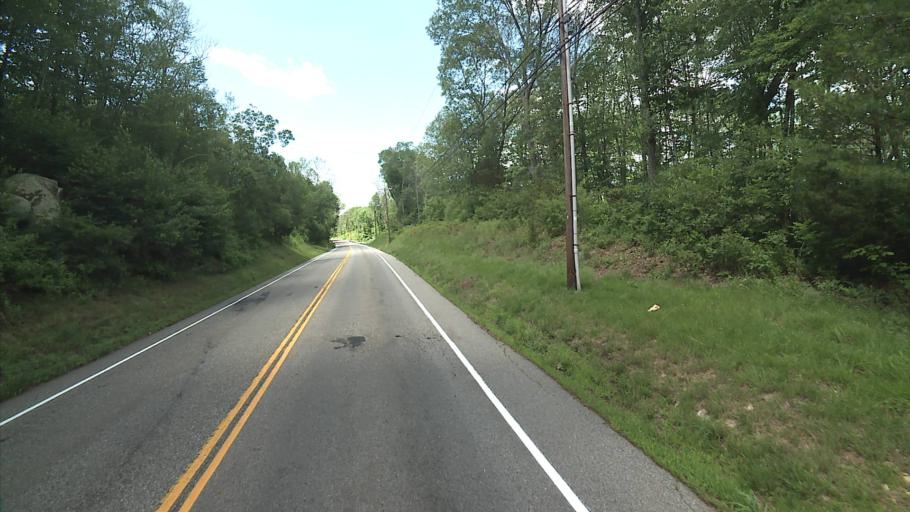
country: US
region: Connecticut
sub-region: New London County
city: Old Mystic
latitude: 41.4038
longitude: -71.9462
